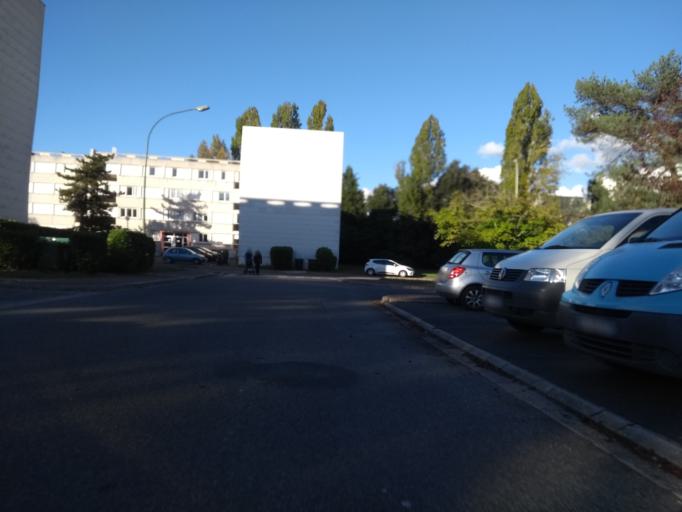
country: FR
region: Aquitaine
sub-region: Departement de la Gironde
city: Gradignan
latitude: 44.7781
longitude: -0.6075
